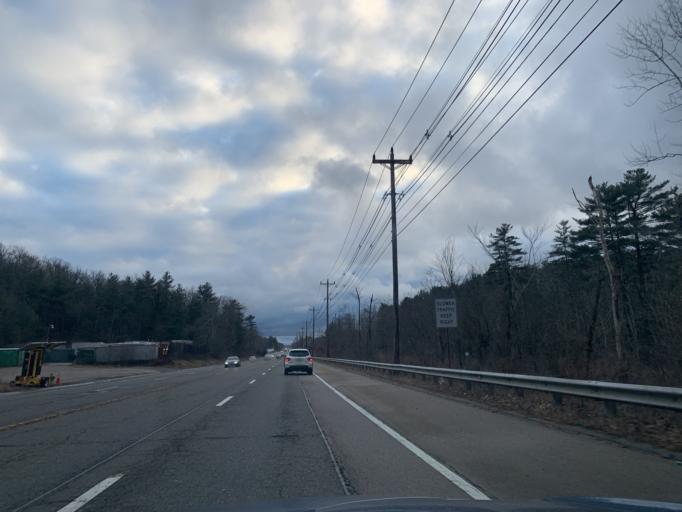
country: US
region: Massachusetts
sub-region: Norfolk County
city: Wrentham
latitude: 42.0642
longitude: -71.2944
